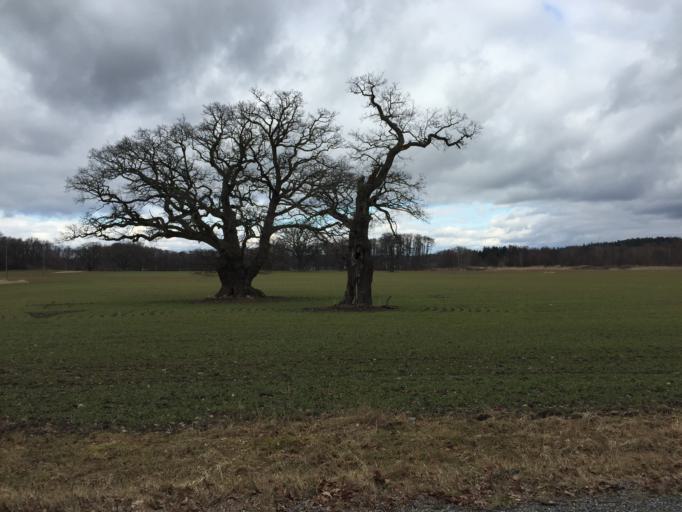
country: SE
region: Stockholm
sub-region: Botkyrka Kommun
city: Eriksberg
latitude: 59.2505
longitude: 17.7787
